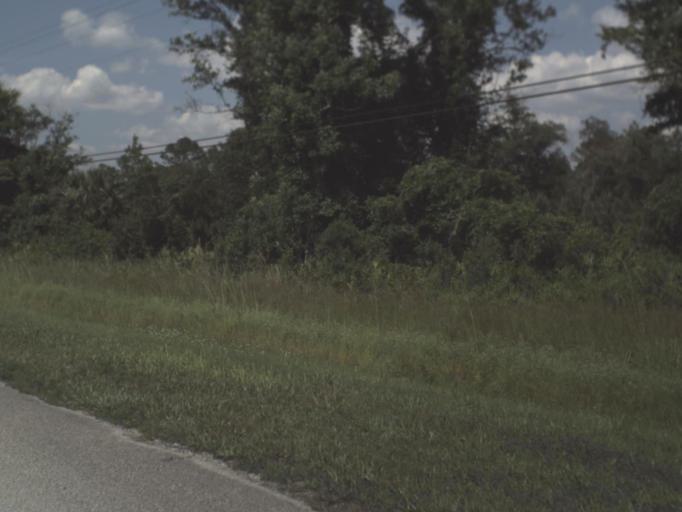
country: US
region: Florida
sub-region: Alachua County
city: Hawthorne
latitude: 29.5665
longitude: -82.0933
